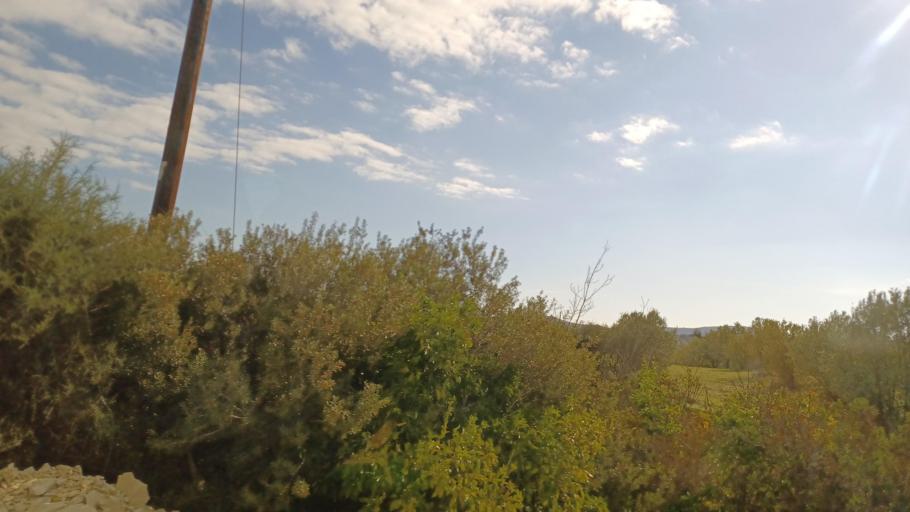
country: CY
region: Larnaka
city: Kofinou
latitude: 34.8171
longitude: 33.3491
